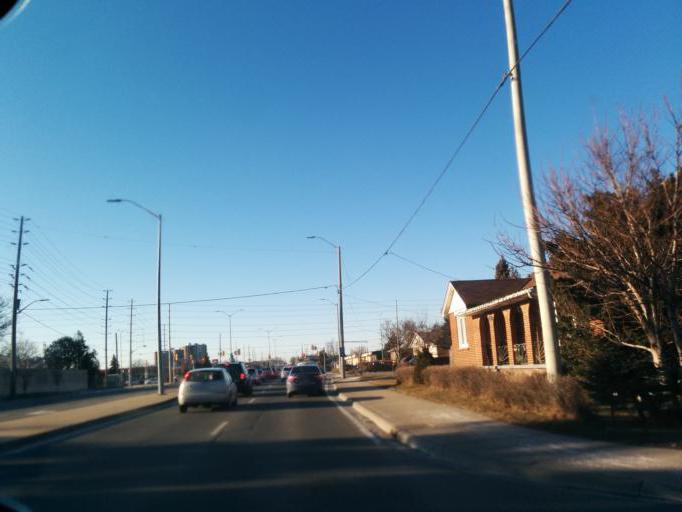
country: CA
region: Ontario
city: Mississauga
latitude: 43.5879
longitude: -79.5902
